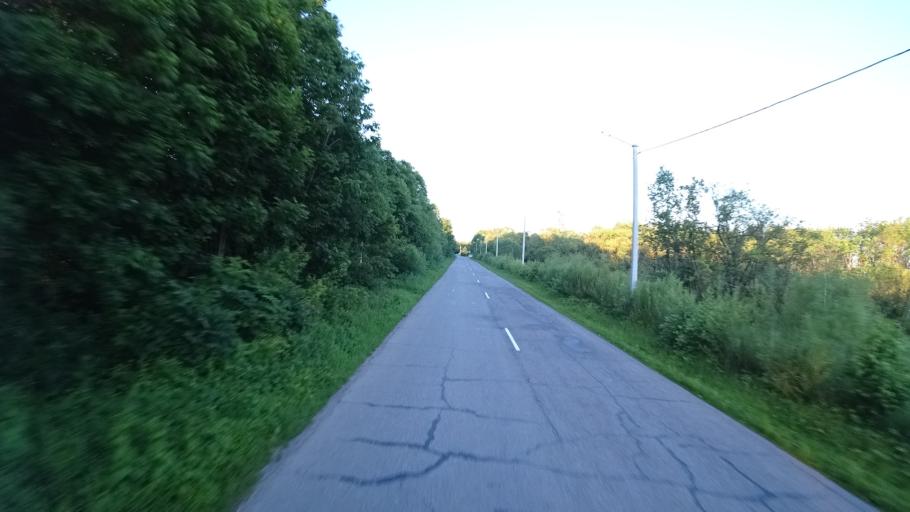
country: RU
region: Khabarovsk Krai
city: Khor
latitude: 47.8531
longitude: 134.9780
